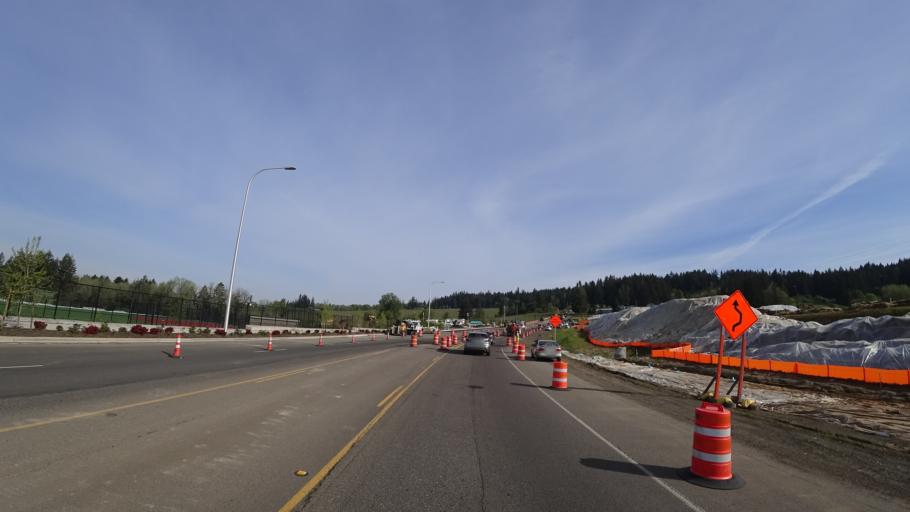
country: US
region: Oregon
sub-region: Washington County
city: King City
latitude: 45.4302
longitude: -122.8565
